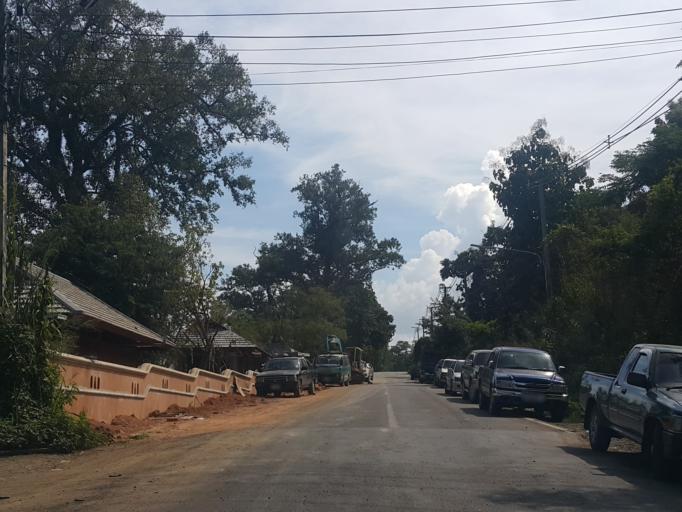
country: TH
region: Chiang Mai
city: Mae On
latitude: 18.8282
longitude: 99.2097
